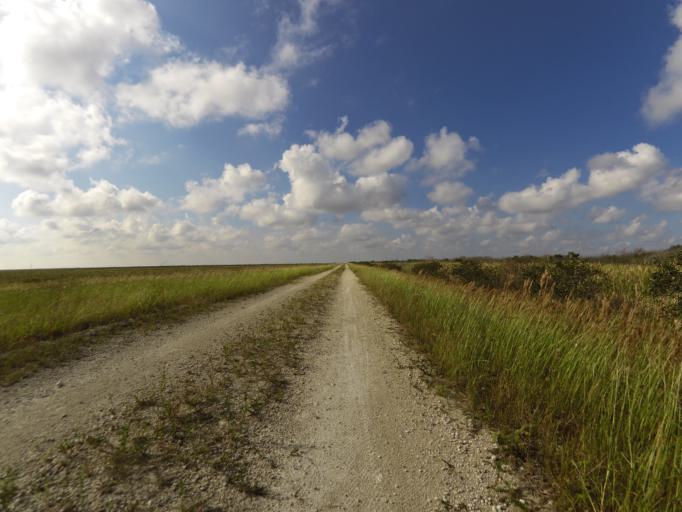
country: US
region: Florida
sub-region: Broward County
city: Weston
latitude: 26.0384
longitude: -80.4895
